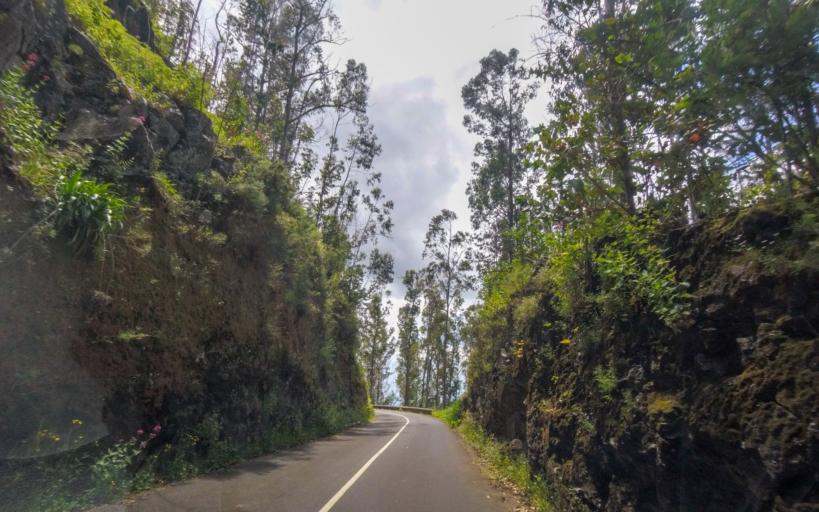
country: PT
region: Madeira
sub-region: Funchal
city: Nossa Senhora do Monte
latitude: 32.6774
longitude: -16.8824
